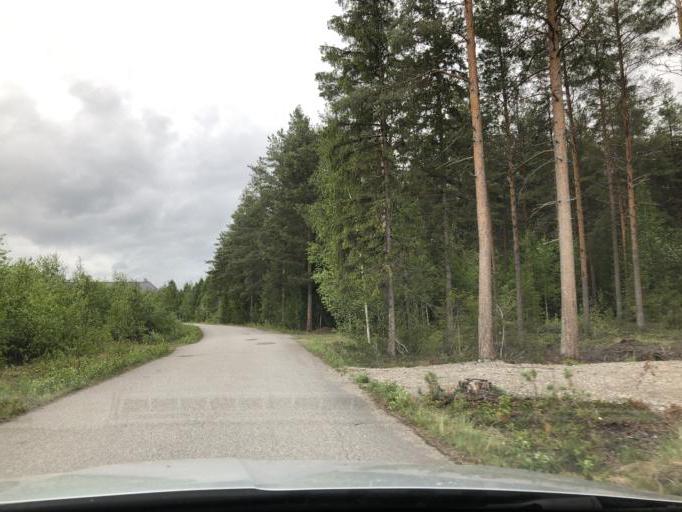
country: SE
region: Norrbotten
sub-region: Pitea Kommun
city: Roknas
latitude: 65.3901
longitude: 21.2696
